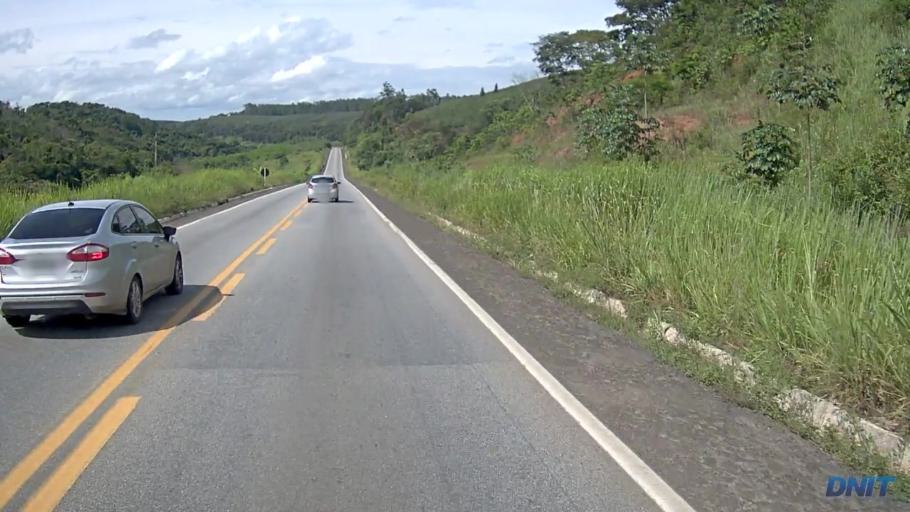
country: BR
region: Minas Gerais
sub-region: Ipaba
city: Ipaba
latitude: -19.4127
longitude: -42.4903
